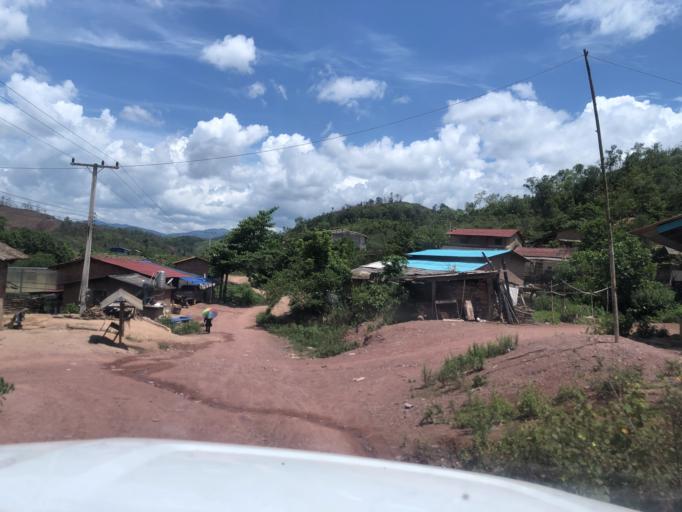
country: CN
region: Yunnan
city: Menglie
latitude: 22.2470
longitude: 101.6082
